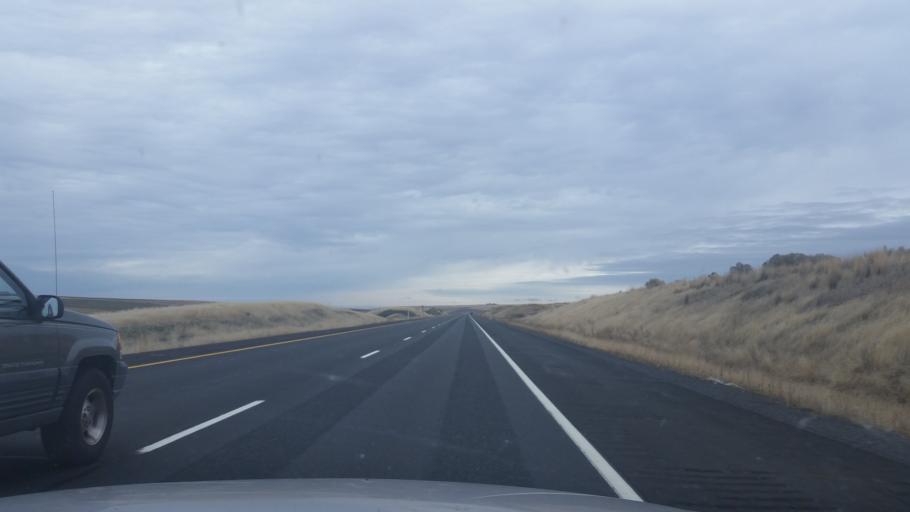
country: US
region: Washington
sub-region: Adams County
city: Ritzville
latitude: 47.0989
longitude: -118.6158
